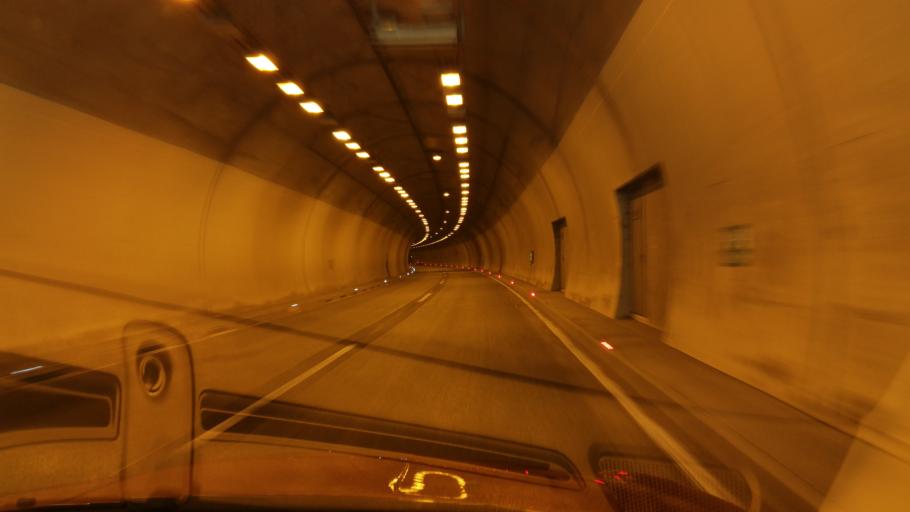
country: AT
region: Upper Austria
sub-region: Politischer Bezirk Kirchdorf an der Krems
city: Micheldorf in Oberoesterreich
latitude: 47.8459
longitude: 14.1694
